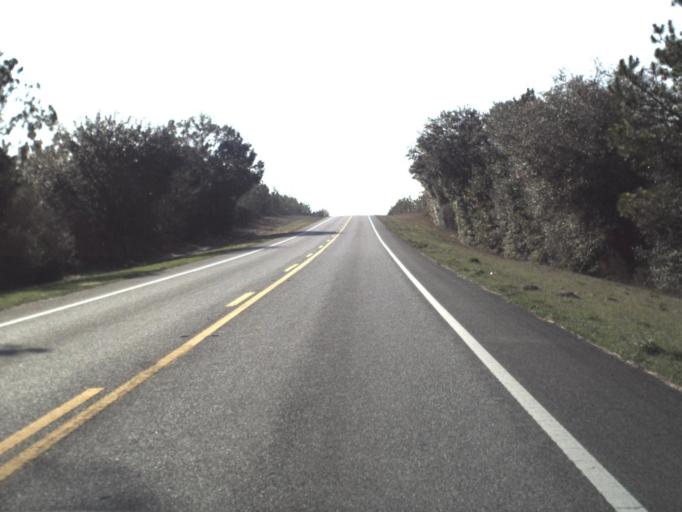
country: US
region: Florida
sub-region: Bay County
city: Youngstown
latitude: 30.4279
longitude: -85.5880
